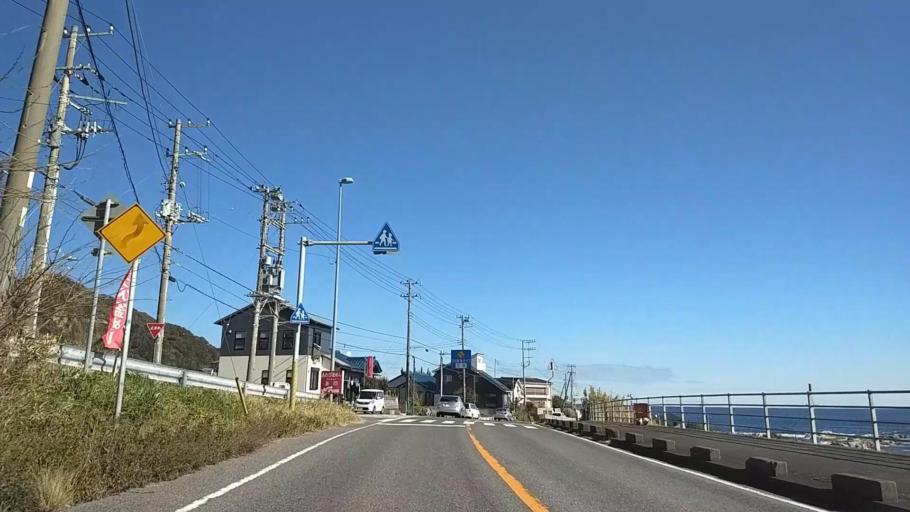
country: JP
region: Chiba
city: Kawaguchi
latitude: 35.0695
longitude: 140.0814
